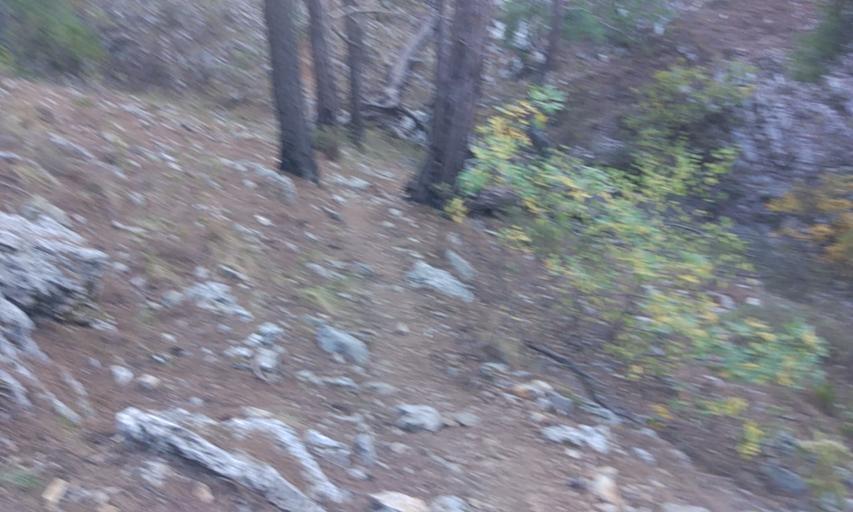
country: TR
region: Antalya
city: Tekirova
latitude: 36.3634
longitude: 30.4791
